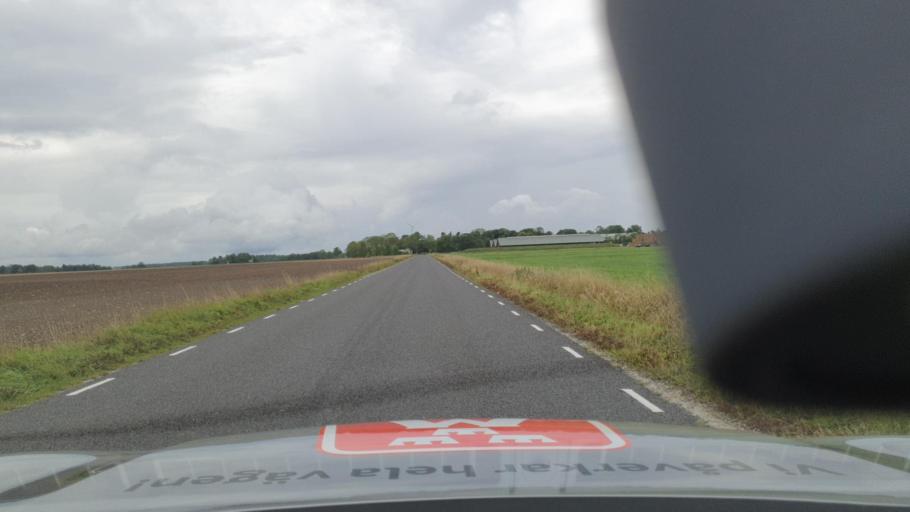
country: SE
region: Gotland
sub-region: Gotland
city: Visby
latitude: 57.5556
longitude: 18.4513
